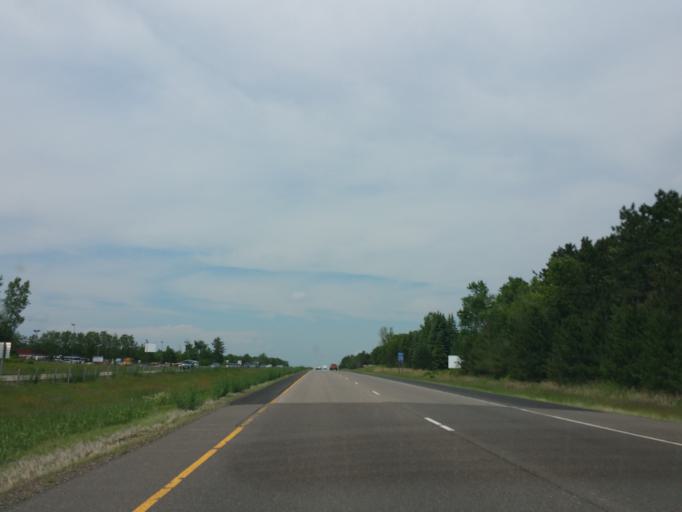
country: US
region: Minnesota
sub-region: Chisago County
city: North Branch
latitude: 45.5160
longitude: -92.9924
